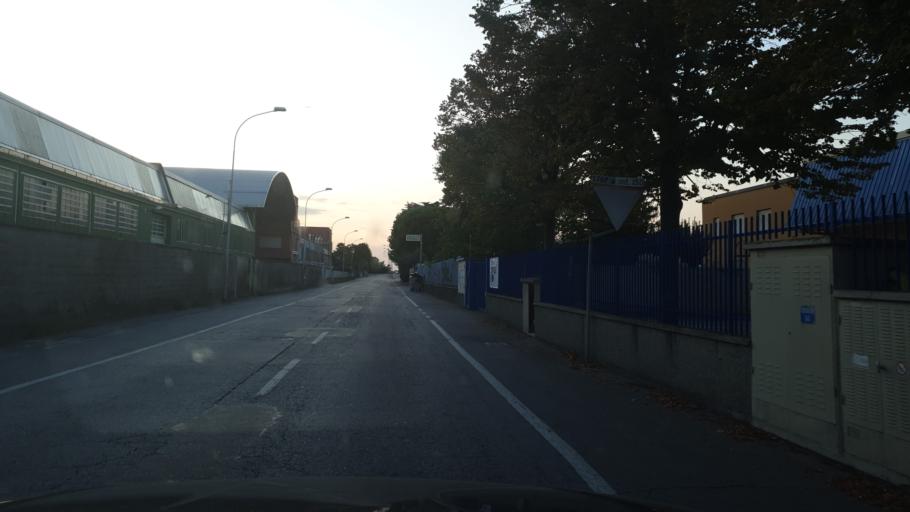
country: IT
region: Emilia-Romagna
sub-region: Provincia di Bologna
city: Quarto Inferiore
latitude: 44.5496
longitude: 11.3914
